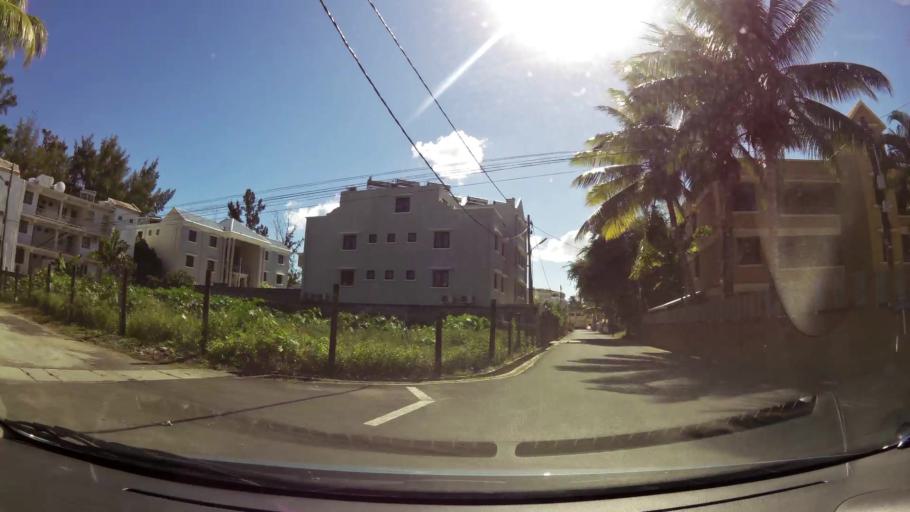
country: MU
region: Black River
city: Flic en Flac
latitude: -20.2866
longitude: 57.3647
